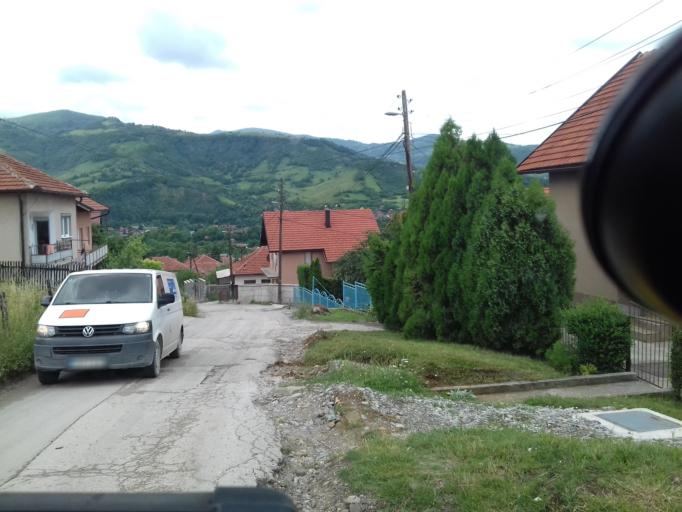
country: BA
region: Federation of Bosnia and Herzegovina
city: Zenica
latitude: 44.1993
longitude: 17.9279
